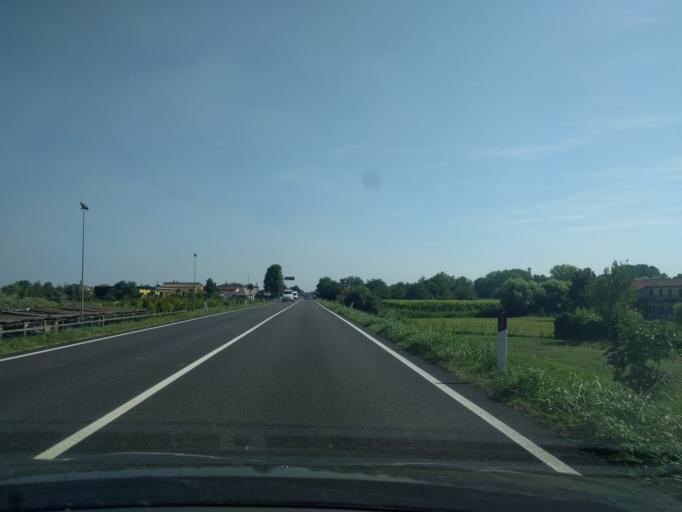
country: IT
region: Veneto
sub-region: Provincia di Padova
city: Solesino
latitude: 45.1923
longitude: 11.7558
